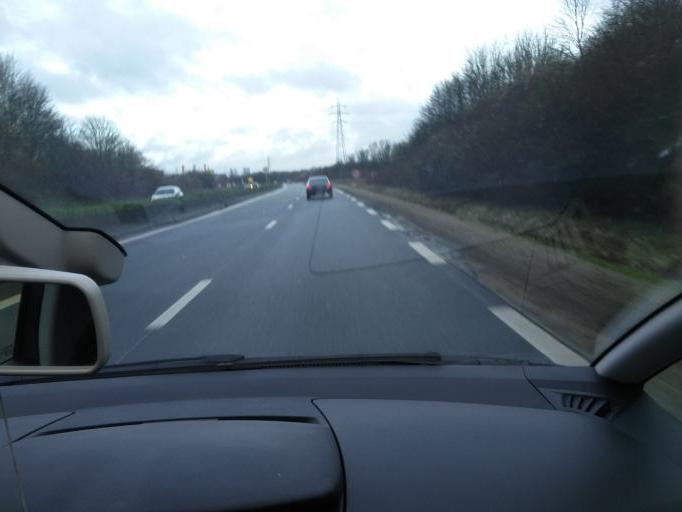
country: FR
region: Picardie
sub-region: Departement de la Somme
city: Rivery
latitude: 49.9137
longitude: 2.3424
